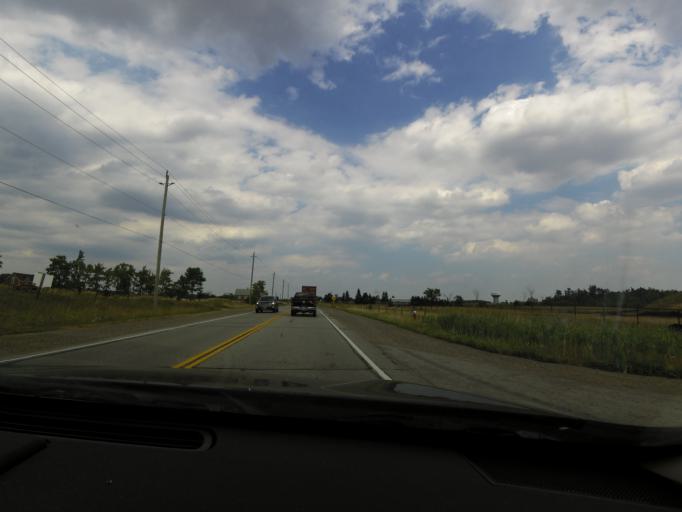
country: CA
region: Ontario
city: Brampton
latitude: 43.7760
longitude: -79.8755
